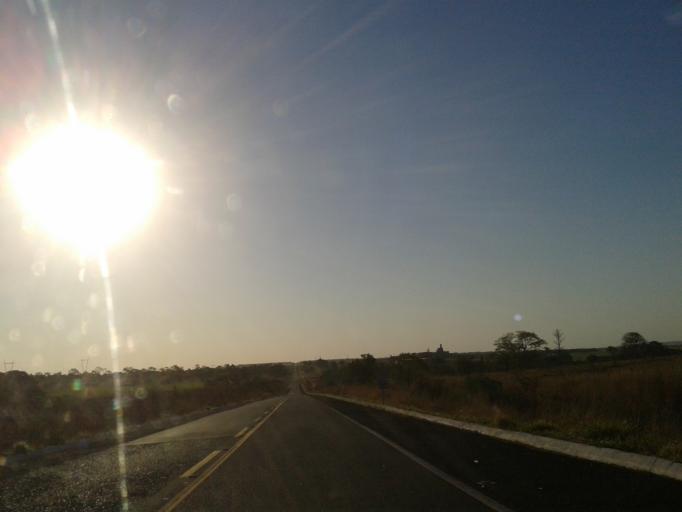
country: BR
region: Minas Gerais
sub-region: Santa Vitoria
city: Santa Vitoria
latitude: -19.0818
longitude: -50.3576
